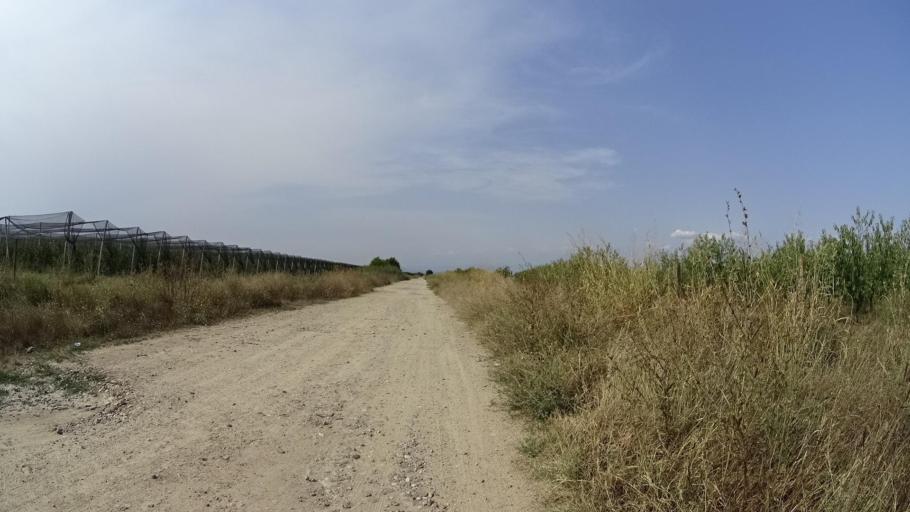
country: BG
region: Plovdiv
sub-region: Obshtina Kaloyanovo
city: Kaloyanovo
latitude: 42.2790
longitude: 24.7994
